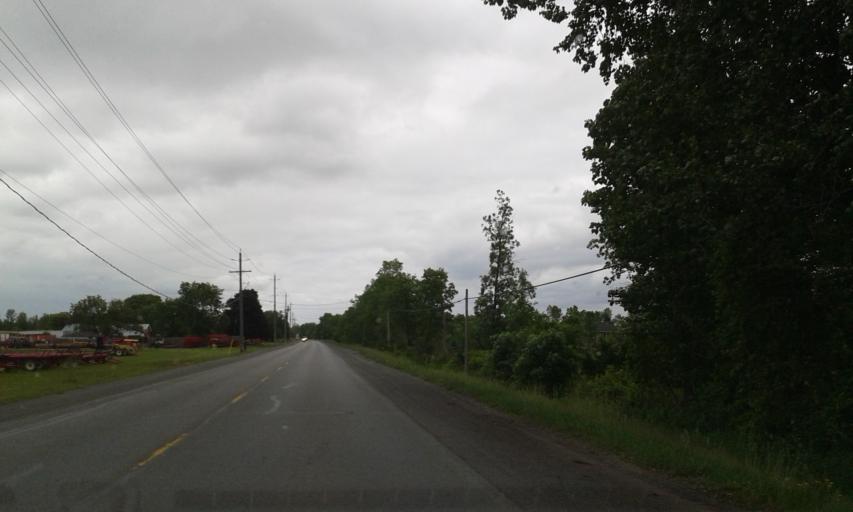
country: CA
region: Ontario
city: Skatepark
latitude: 44.2544
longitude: -76.7884
